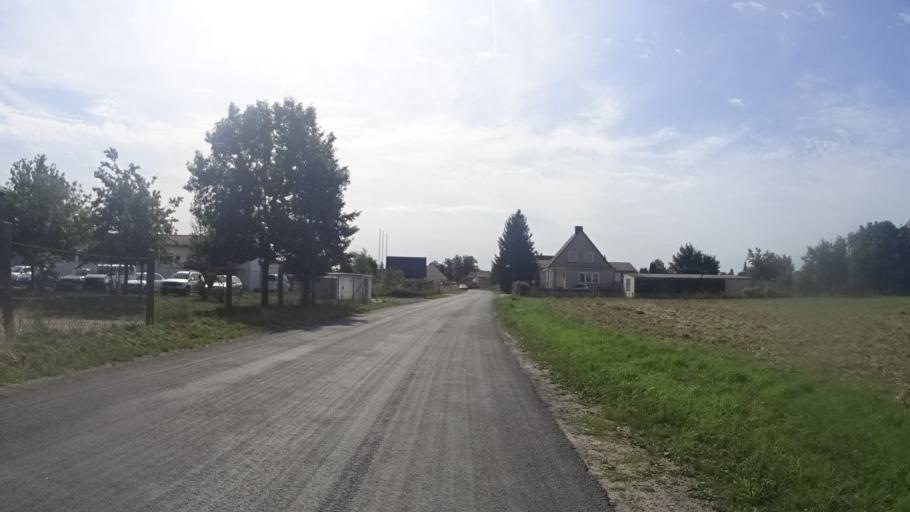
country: DE
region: Brandenburg
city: Golzow
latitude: 52.3103
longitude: 12.6958
